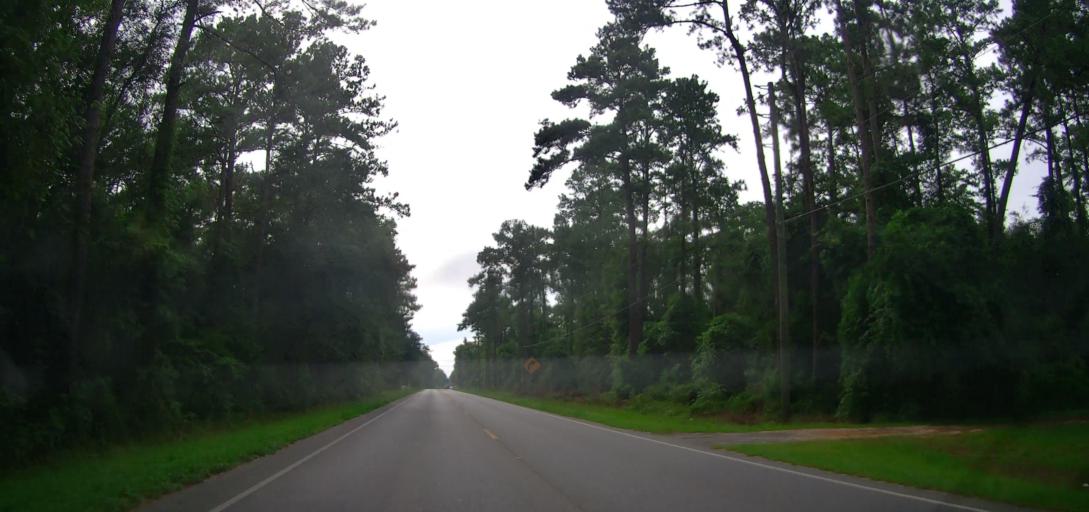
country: US
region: Georgia
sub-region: Wayne County
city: Jesup
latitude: 31.6626
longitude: -81.8551
